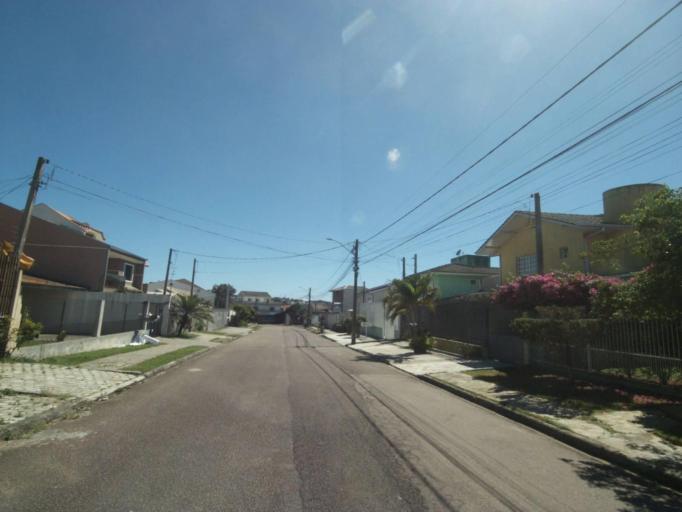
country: BR
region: Parana
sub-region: Curitiba
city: Curitiba
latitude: -25.4826
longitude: -49.3383
